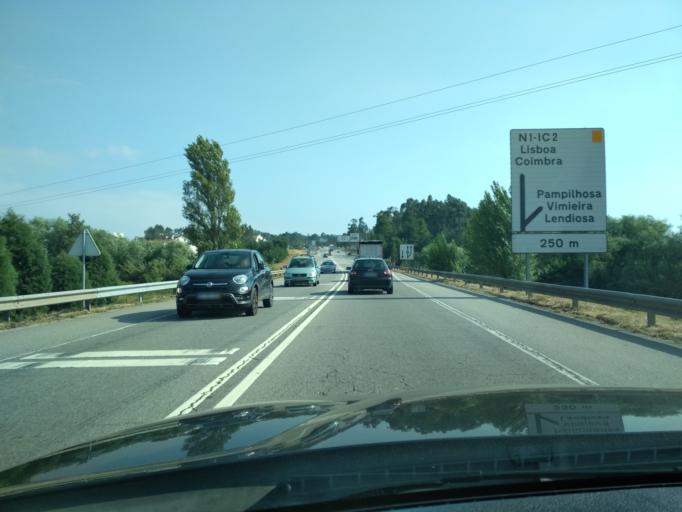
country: PT
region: Aveiro
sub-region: Mealhada
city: Mealhada
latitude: 40.3570
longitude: -8.4512
